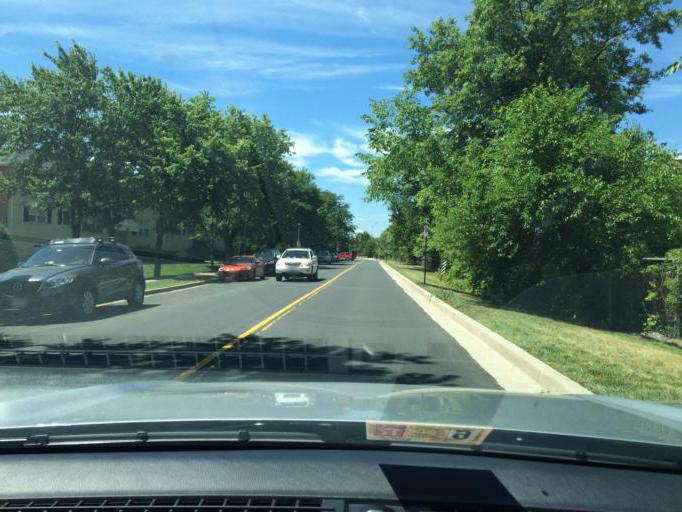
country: US
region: Virginia
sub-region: Arlington County
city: Arlington
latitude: 38.8501
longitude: -77.0761
